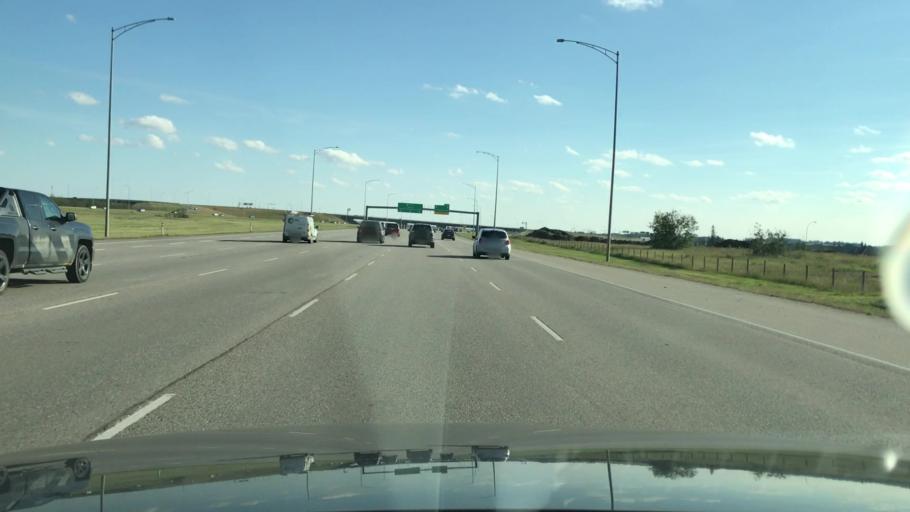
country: CA
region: Alberta
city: Beaumont
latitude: 53.4061
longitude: -113.5061
